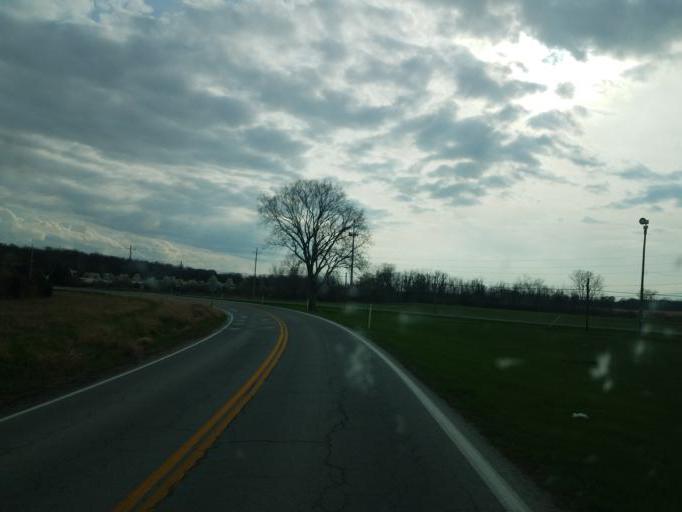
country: US
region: Ohio
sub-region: Erie County
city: Sandusky
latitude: 41.5155
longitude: -82.7605
